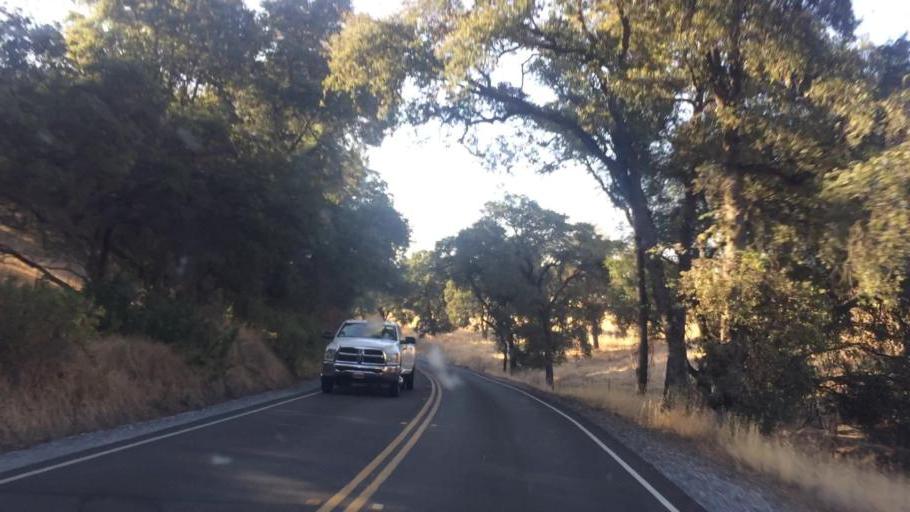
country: US
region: California
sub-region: Amador County
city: Plymouth
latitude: 38.5054
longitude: -120.9440
